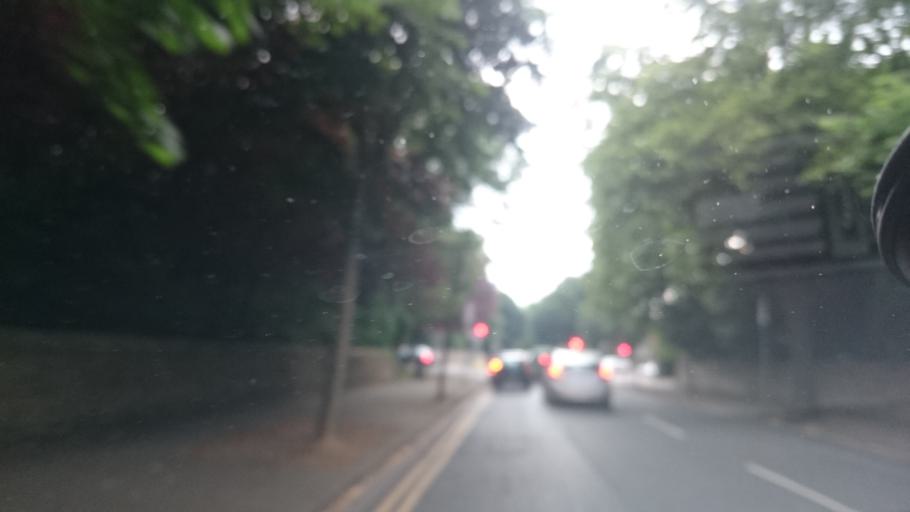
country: IE
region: Leinster
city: Donnybrook
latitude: 53.3205
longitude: -6.2144
